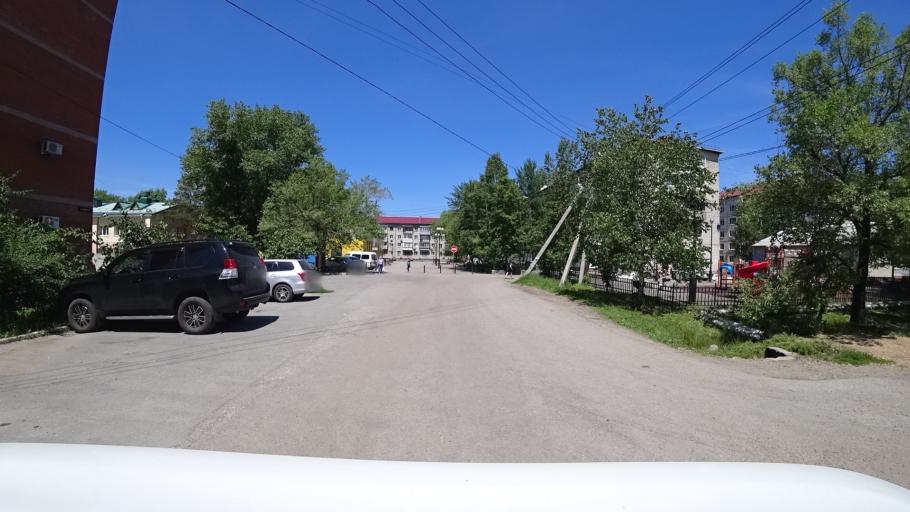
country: RU
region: Khabarovsk Krai
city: Topolevo
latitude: 48.5064
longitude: 135.1750
